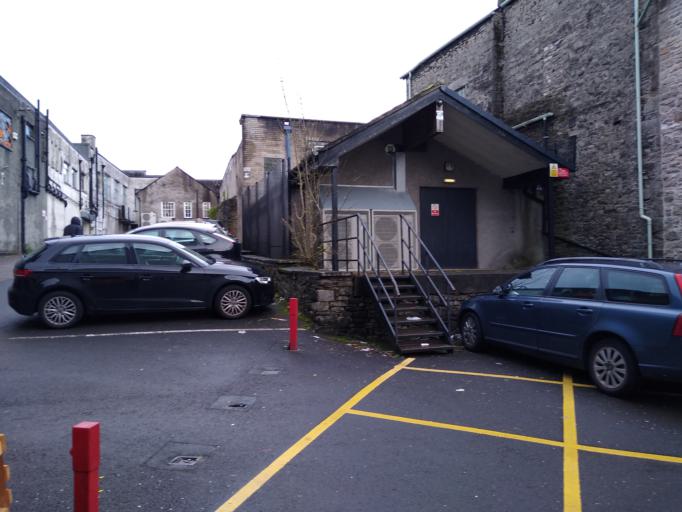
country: GB
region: England
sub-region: Cumbria
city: Kendal
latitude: 54.3280
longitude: -2.7484
